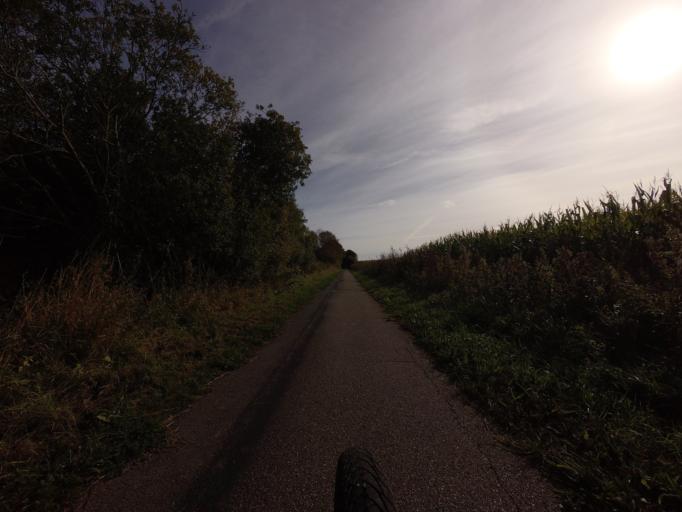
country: DK
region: Central Jutland
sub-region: Viborg Kommune
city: Viborg
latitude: 56.4383
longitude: 9.4917
